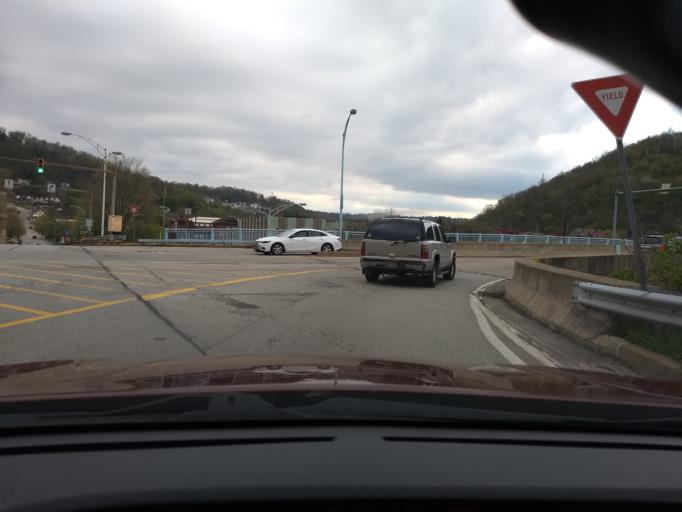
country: US
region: Pennsylvania
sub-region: Allegheny County
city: Wilmerding
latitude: 40.3932
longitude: -79.8048
